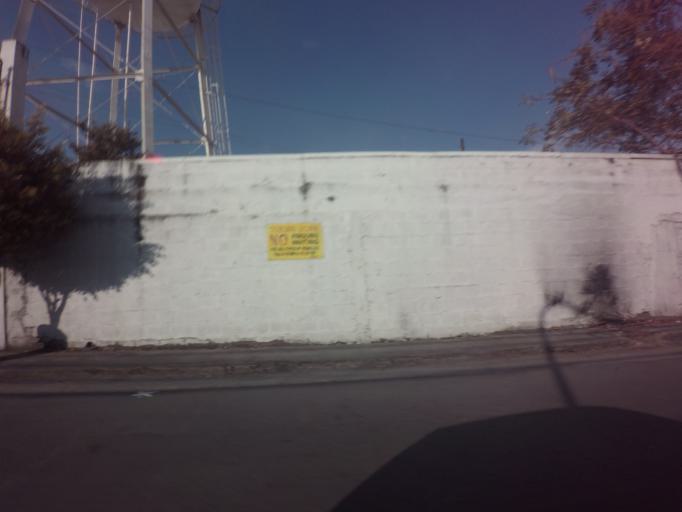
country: PH
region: Calabarzon
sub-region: Province of Rizal
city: Taguig
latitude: 14.4805
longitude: 121.0501
